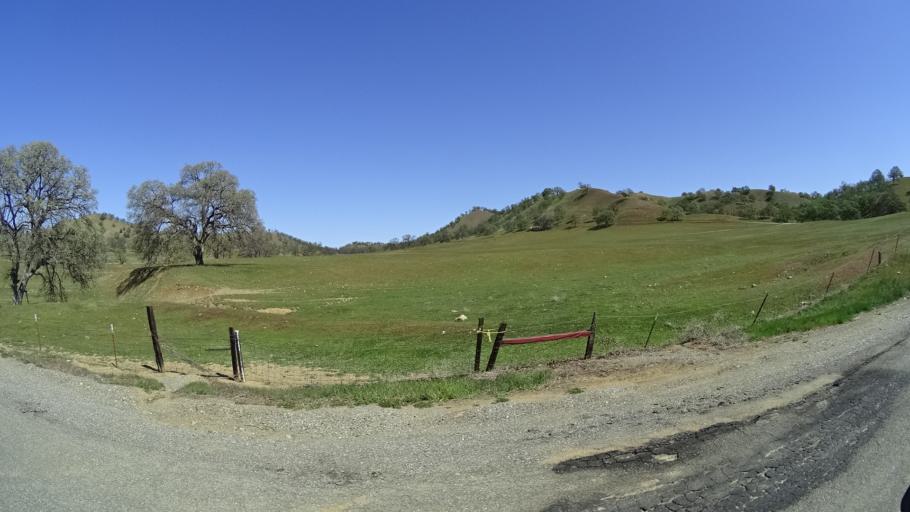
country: US
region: California
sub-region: Tehama County
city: Rancho Tehama Reserve
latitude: 39.7886
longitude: -122.4877
